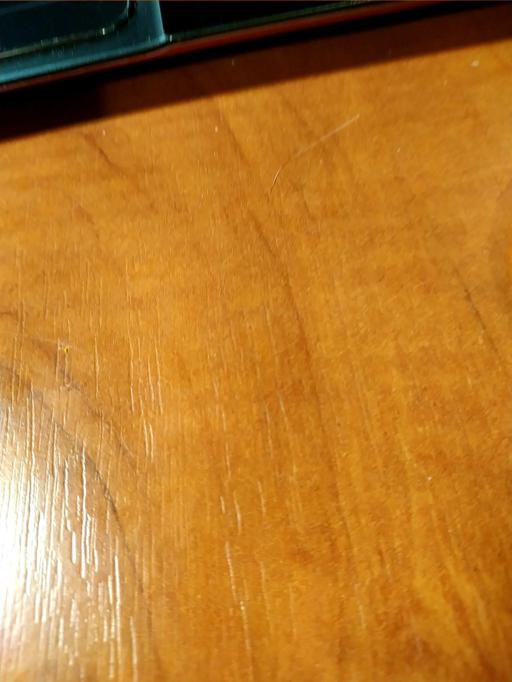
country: RU
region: Smolensk
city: Yartsevo
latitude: 55.4118
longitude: 32.8340
